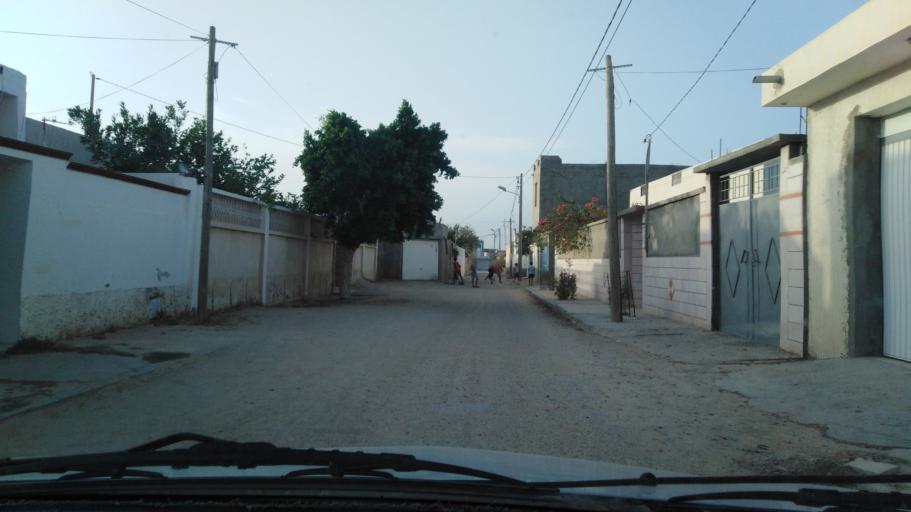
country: TN
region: Qabis
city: Gabes
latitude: 33.9544
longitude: 9.9962
